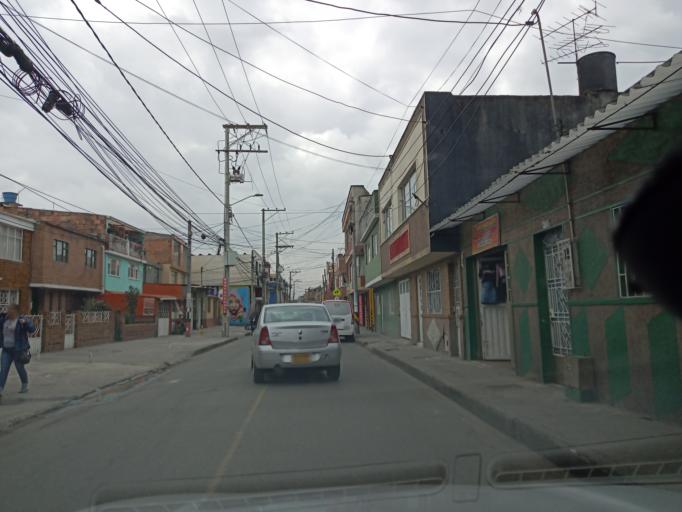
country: CO
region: Cundinamarca
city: Funza
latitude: 4.6717
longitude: -74.1480
